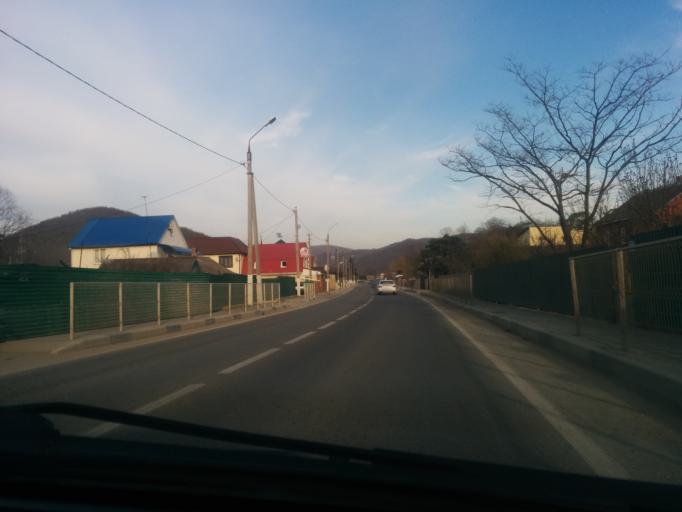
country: RU
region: Krasnodarskiy
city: Novomikhaylovskiy
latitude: 44.2579
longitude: 38.8586
